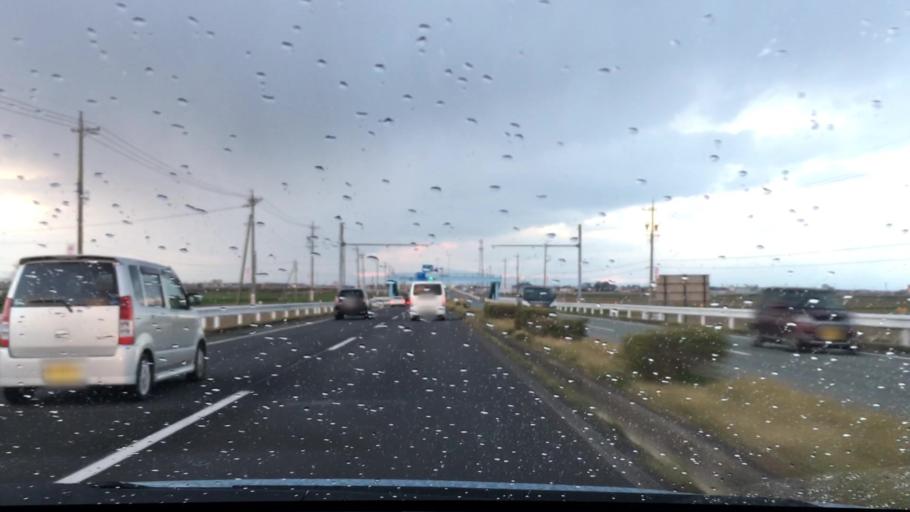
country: JP
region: Mie
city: Ise
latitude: 34.5591
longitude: 136.6465
